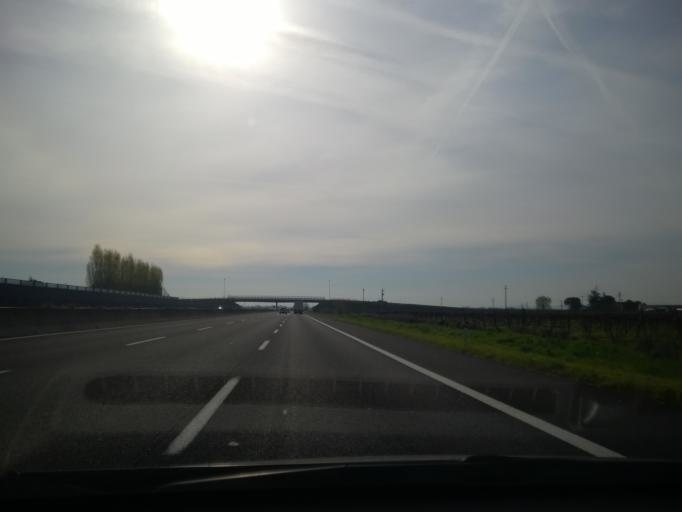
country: IT
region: Emilia-Romagna
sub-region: Provincia di Ravenna
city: Granarolo
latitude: 44.2990
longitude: 11.9657
